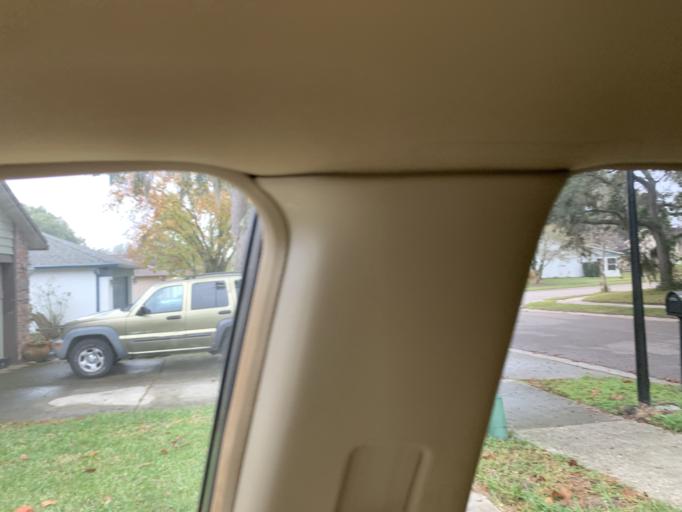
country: US
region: Florida
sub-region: Seminole County
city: Oviedo
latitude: 28.6449
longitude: -81.1858
